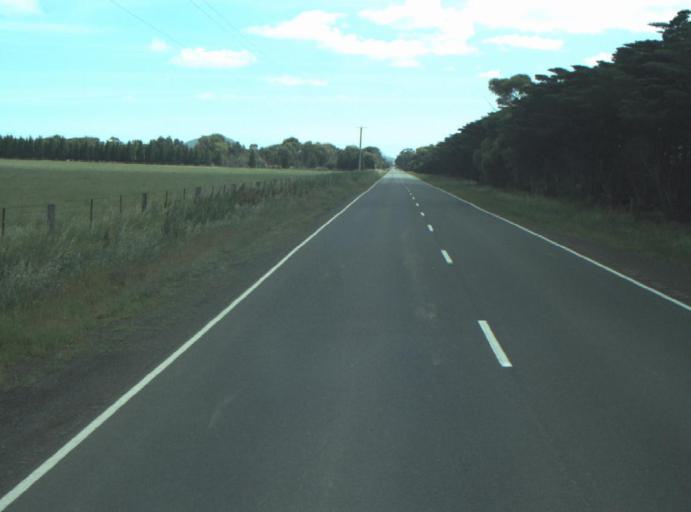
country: AU
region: Victoria
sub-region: Greater Geelong
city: Lara
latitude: -38.0517
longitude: 144.4283
